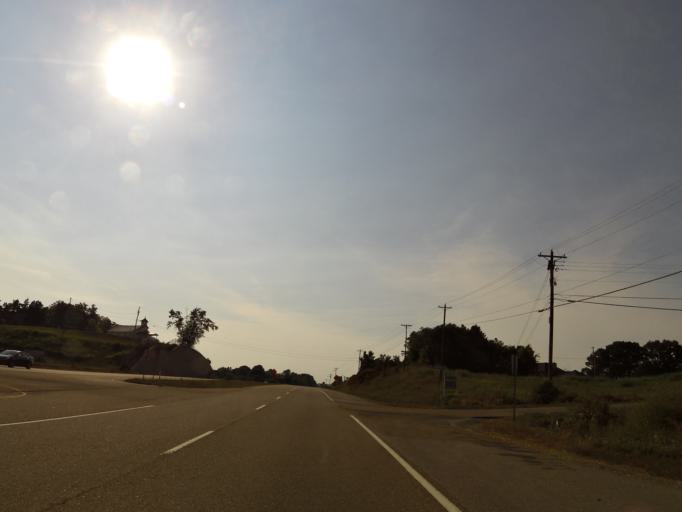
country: US
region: Tennessee
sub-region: Loudon County
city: Lenoir City
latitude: 35.7751
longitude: -84.2346
